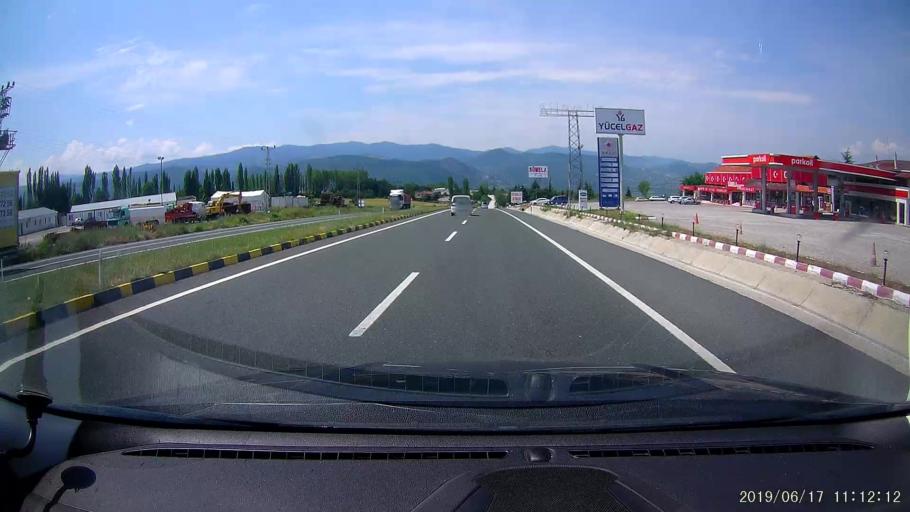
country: TR
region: Kastamonu
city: Tosya
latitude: 40.9754
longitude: 33.9991
